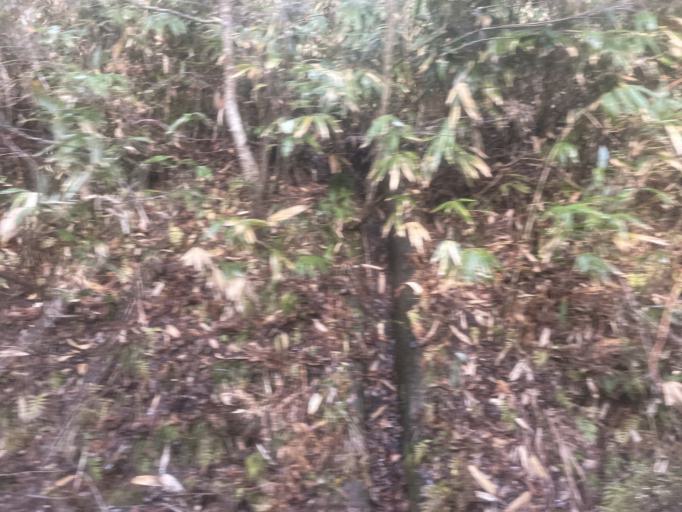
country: JP
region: Aomori
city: Goshogawara
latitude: 41.0787
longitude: 140.5295
